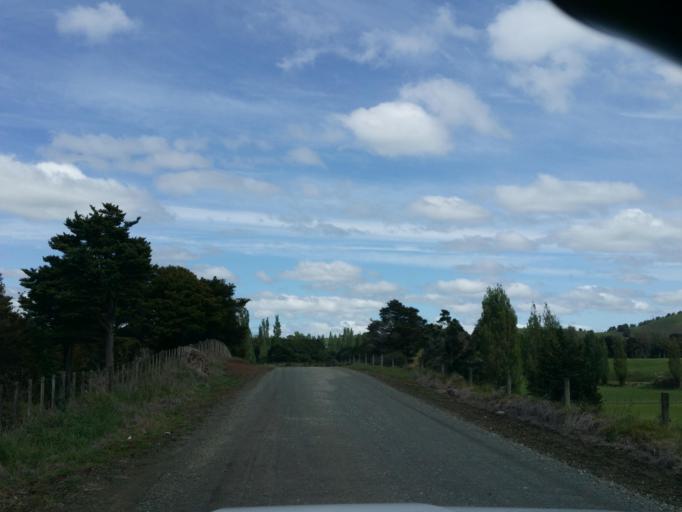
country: NZ
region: Northland
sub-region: Whangarei
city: Maungatapere
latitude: -35.9077
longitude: 174.1310
